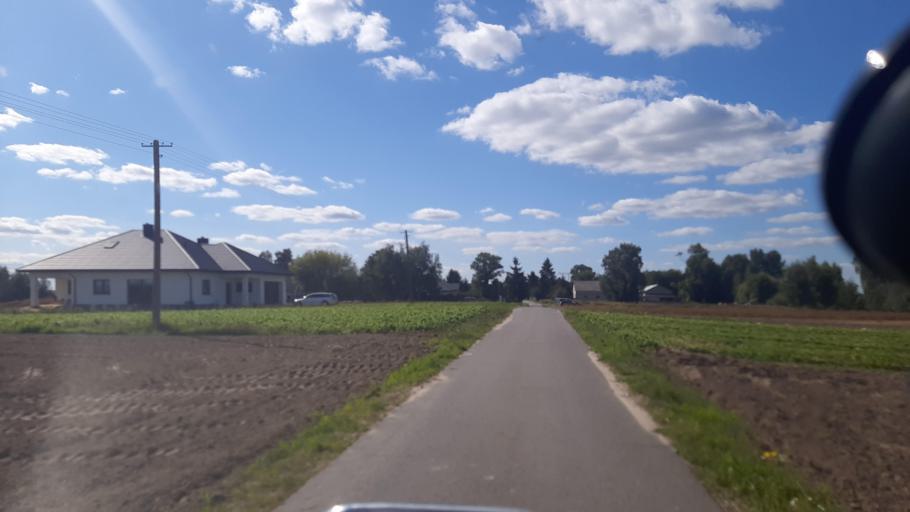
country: PL
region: Lublin Voivodeship
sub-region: Powiat pulawski
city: Markuszow
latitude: 51.3964
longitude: 22.2366
